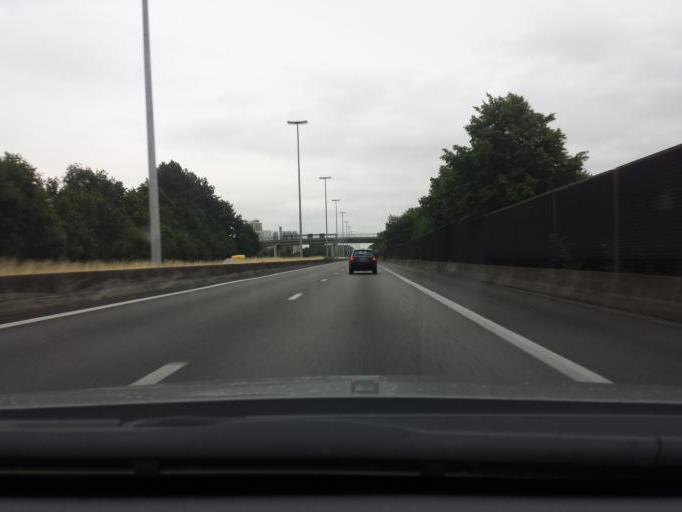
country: BE
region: Flanders
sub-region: Provincie Antwerpen
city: Laakdal
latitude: 51.1126
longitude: 4.9991
